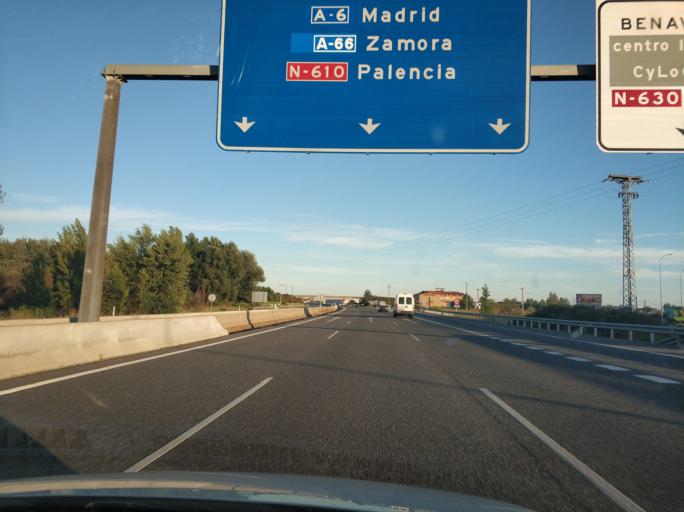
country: ES
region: Castille and Leon
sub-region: Provincia de Zamora
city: Benavente
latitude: 42.0040
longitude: -5.6598
